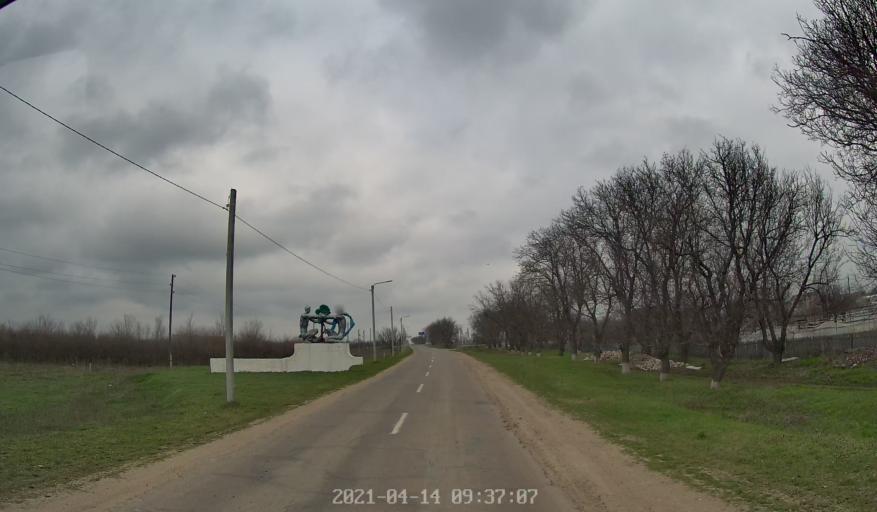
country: MD
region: Chisinau
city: Vadul lui Voda
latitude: 47.1162
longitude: 29.1111
